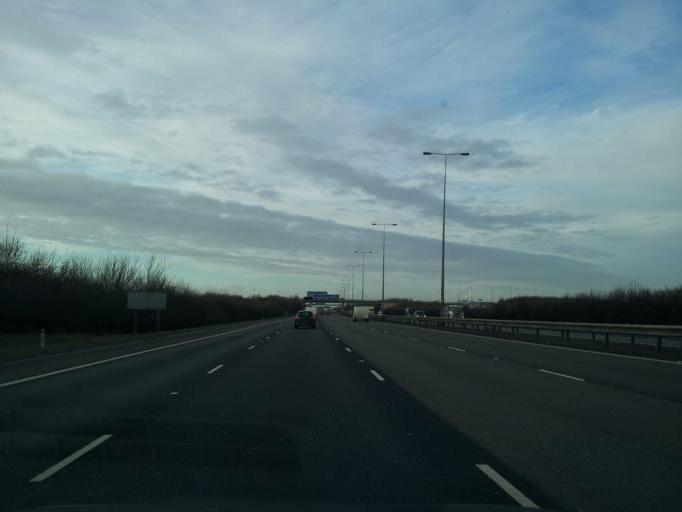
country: GB
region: England
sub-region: Cambridgeshire
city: Sawtry
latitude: 52.4189
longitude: -0.2680
